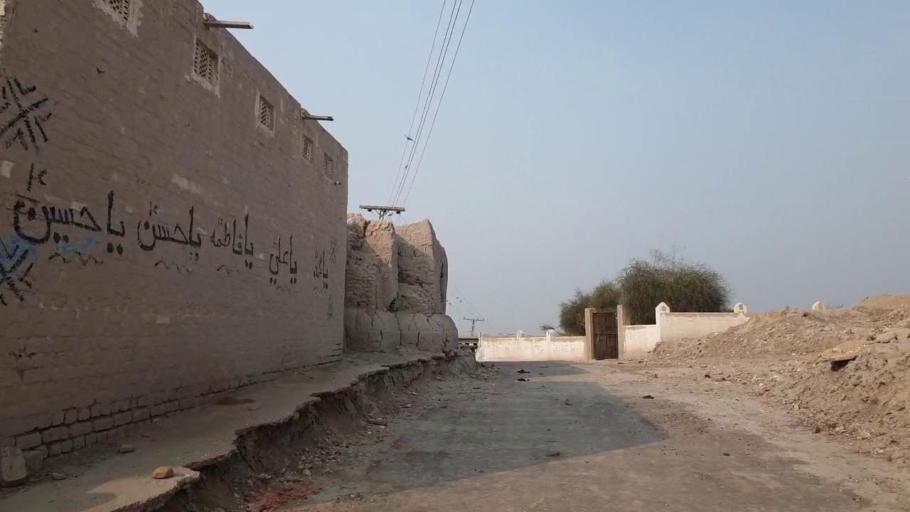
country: PK
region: Sindh
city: Bhan
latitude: 26.4719
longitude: 67.7075
